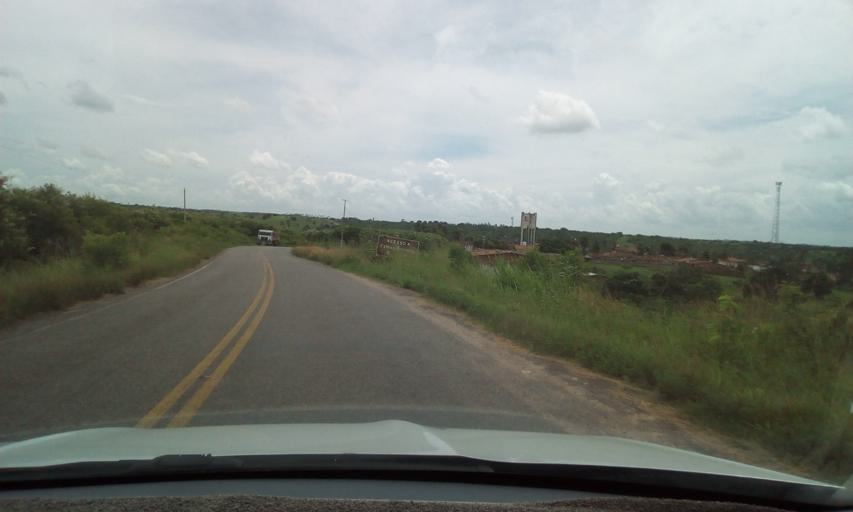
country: BR
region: Paraiba
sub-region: Mari
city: Mari
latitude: -7.1054
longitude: -35.3290
